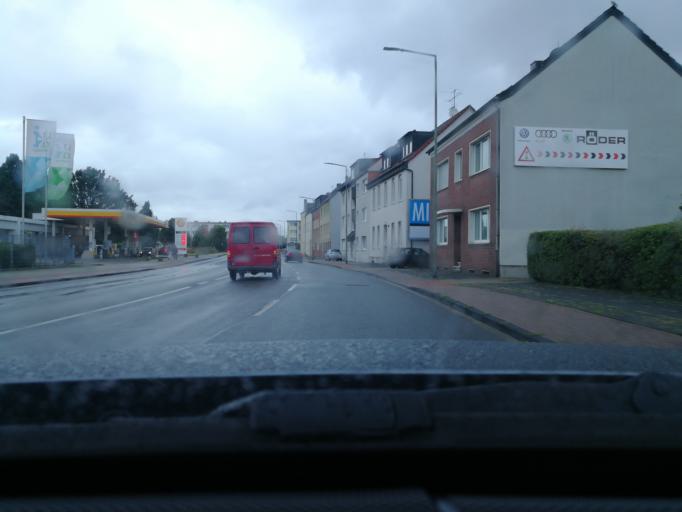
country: DE
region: North Rhine-Westphalia
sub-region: Regierungsbezirk Dusseldorf
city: Dinslaken
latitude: 51.5408
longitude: 6.7373
